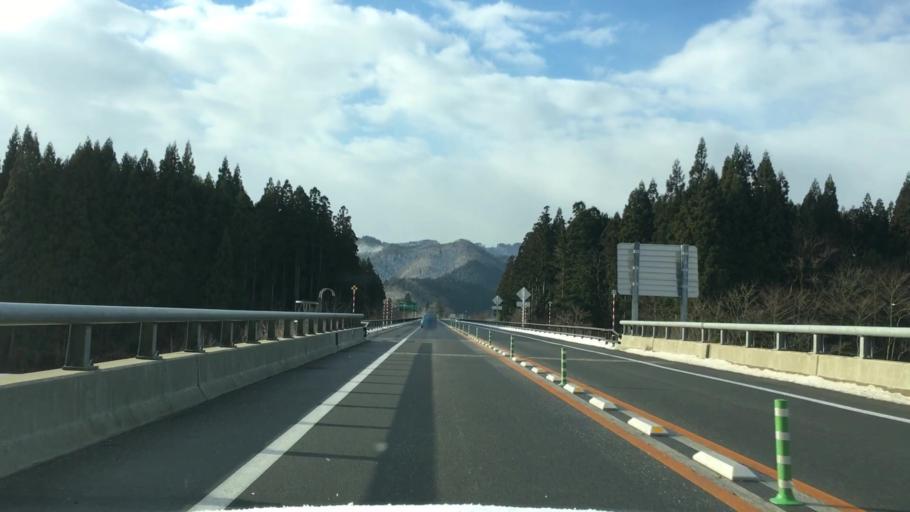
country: JP
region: Akita
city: Odate
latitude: 40.2420
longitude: 140.5074
